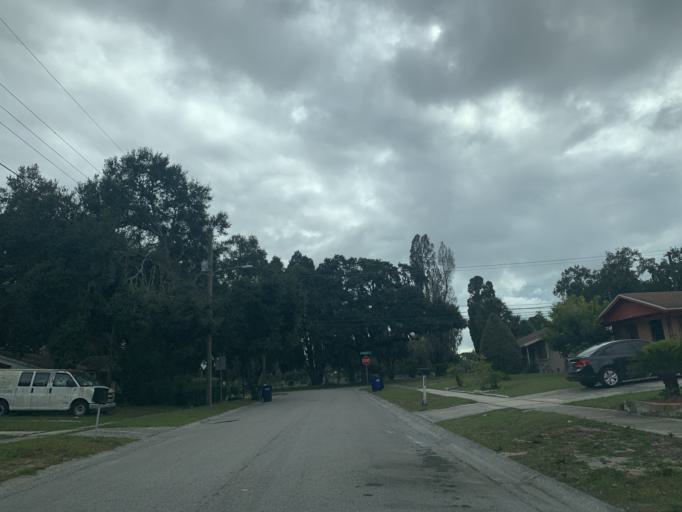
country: US
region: Florida
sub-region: Hillsborough County
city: East Lake-Orient Park
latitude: 27.9857
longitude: -82.4038
